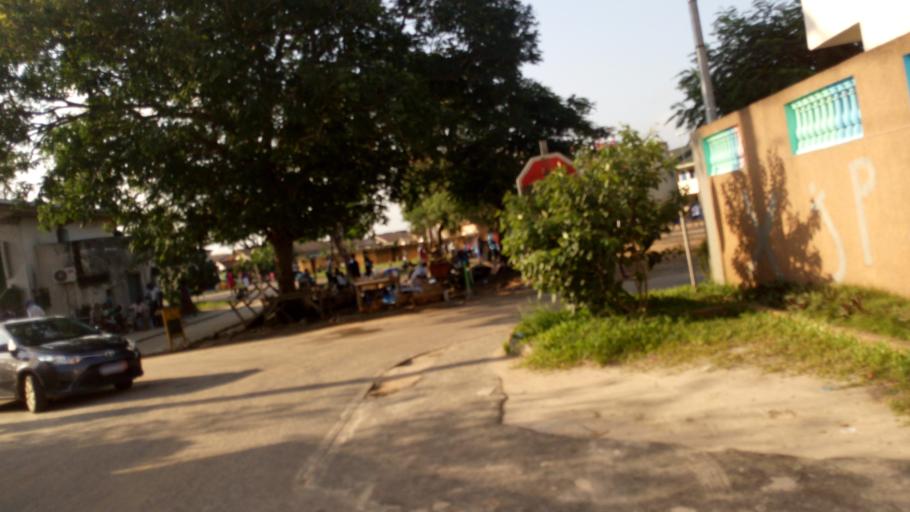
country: CI
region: Lagunes
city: Abobo
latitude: 5.4050
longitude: -3.9804
